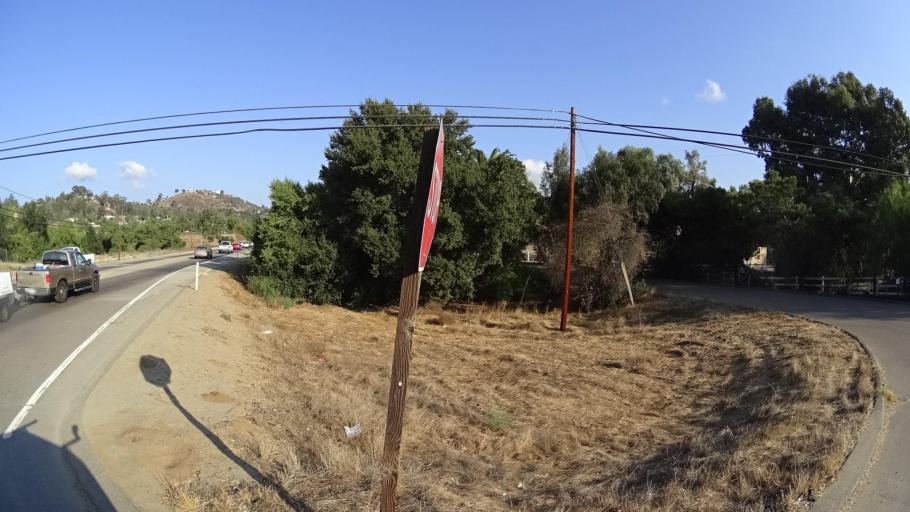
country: US
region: California
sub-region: San Diego County
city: Eucalyptus Hills
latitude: 32.8816
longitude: -116.9278
